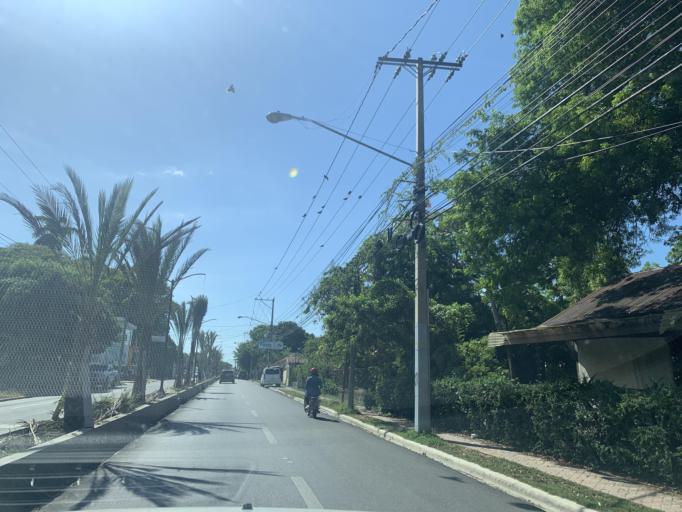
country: DO
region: Puerto Plata
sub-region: Puerto Plata
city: Puerto Plata
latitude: 19.7891
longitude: -70.6781
